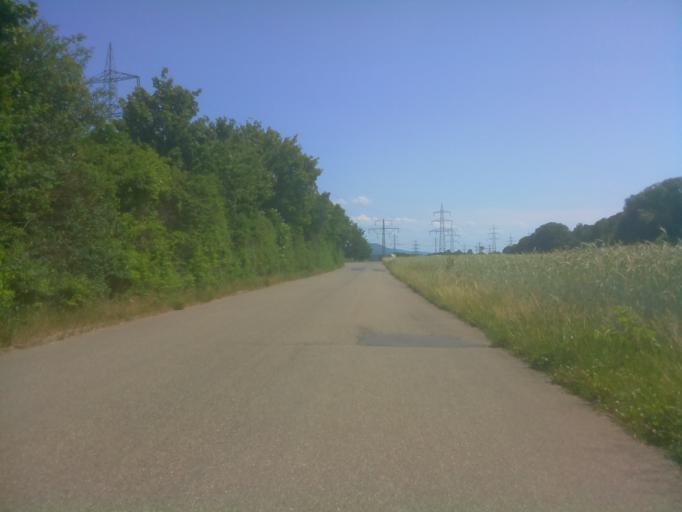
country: DE
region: Hesse
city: Viernheim
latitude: 49.5563
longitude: 8.6190
